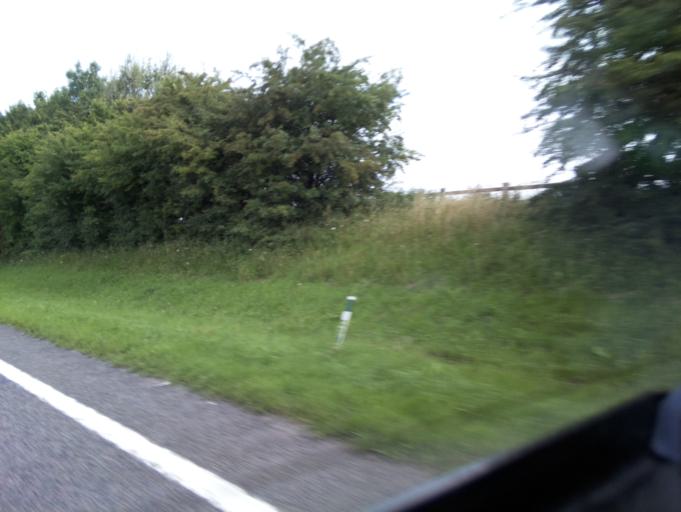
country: GB
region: England
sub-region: Gloucestershire
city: Shurdington
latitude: 51.8238
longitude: -2.0921
